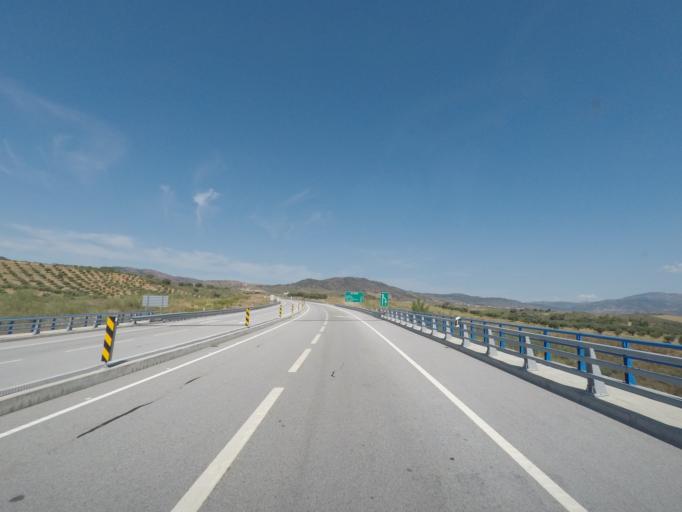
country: PT
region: Braganca
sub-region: Braganca Municipality
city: Vila Flor
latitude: 41.3028
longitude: -7.0737
